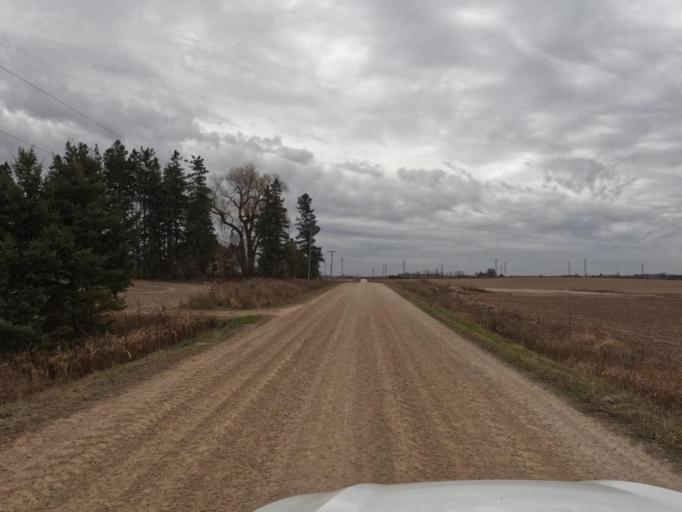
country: CA
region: Ontario
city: Shelburne
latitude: 44.0023
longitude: -80.3874
